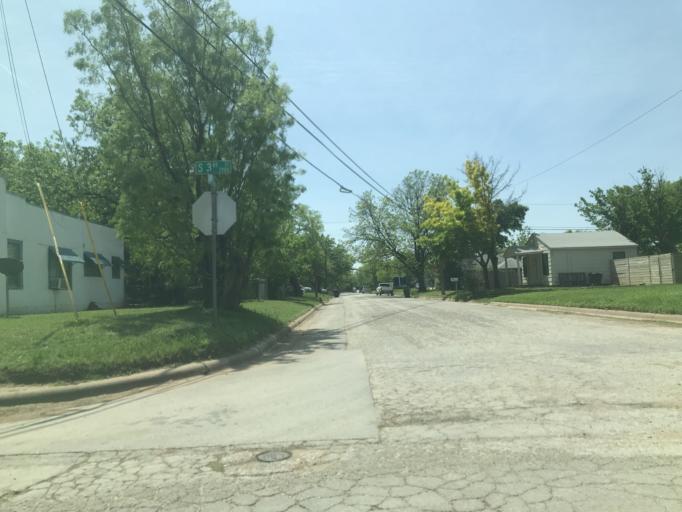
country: US
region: Texas
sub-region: Taylor County
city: Abilene
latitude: 32.4474
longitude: -99.7592
